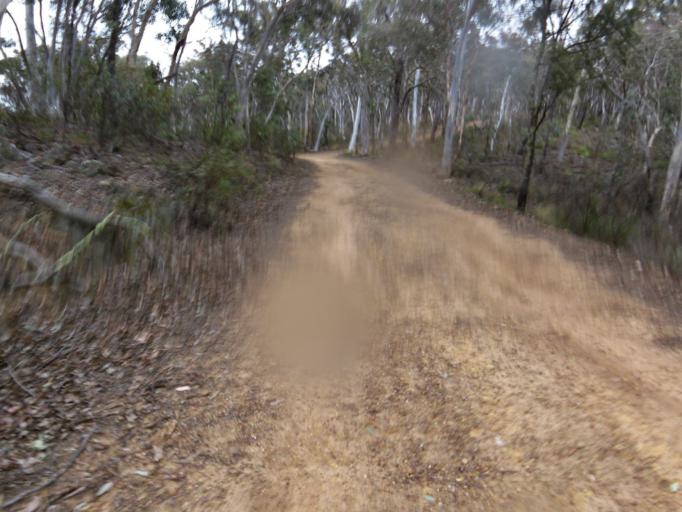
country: AU
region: Australian Capital Territory
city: Acton
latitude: -35.2686
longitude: 149.0991
